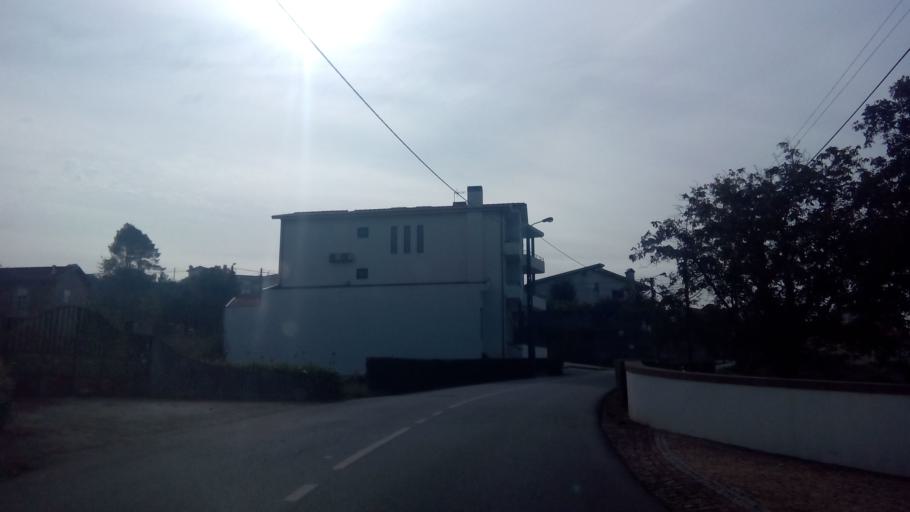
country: PT
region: Porto
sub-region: Paredes
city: Gandra
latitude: 41.1930
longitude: -8.4302
